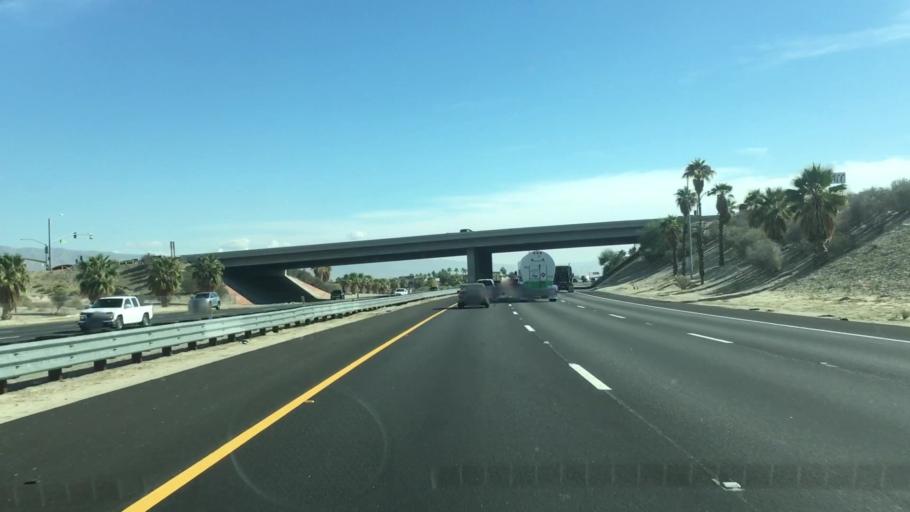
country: US
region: California
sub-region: Riverside County
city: Bermuda Dunes
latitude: 33.7608
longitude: -116.3030
